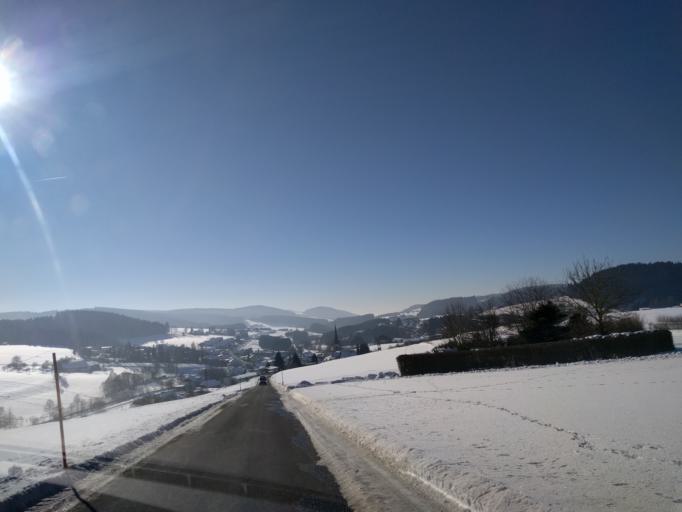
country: AT
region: Upper Austria
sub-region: Politischer Bezirk Urfahr-Umgebung
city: Zwettl an der Rodl
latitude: 48.4717
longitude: 14.2750
